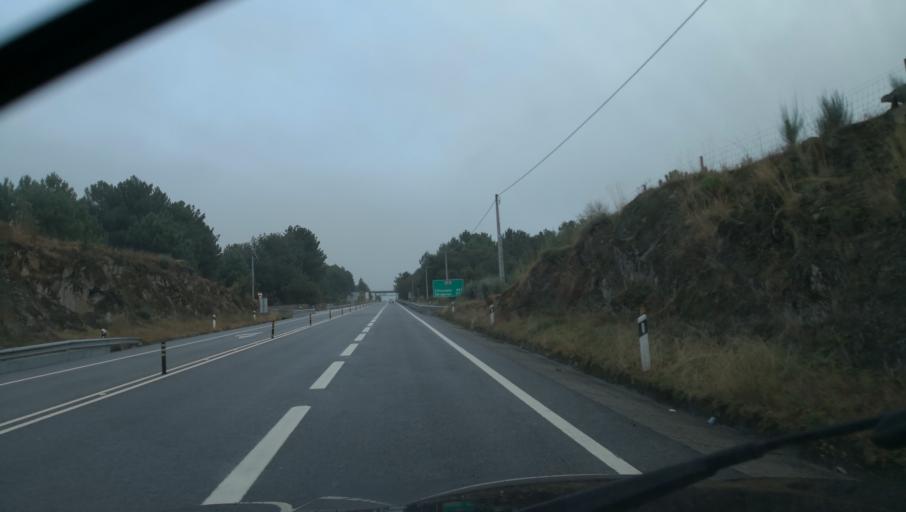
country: PT
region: Vila Real
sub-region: Vila Real
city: Vila Real
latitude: 41.3271
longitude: -7.6715
